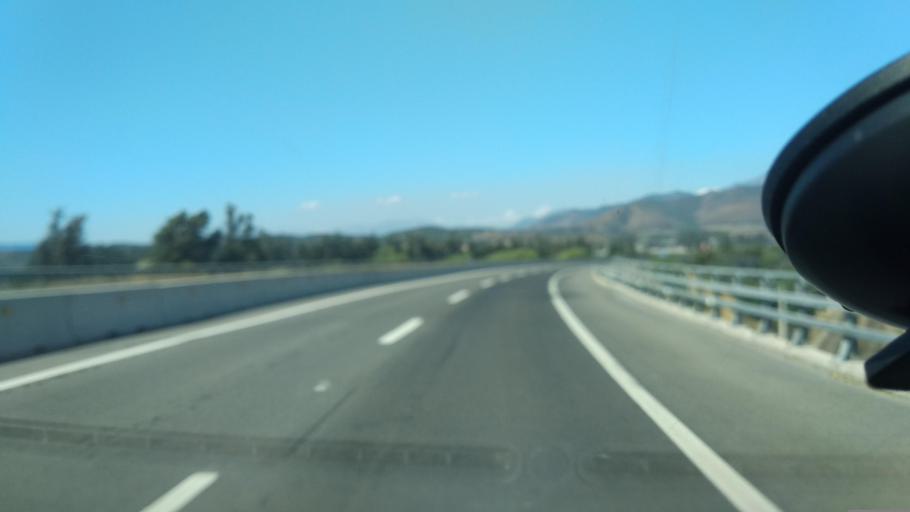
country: CL
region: Valparaiso
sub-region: Provincia de Marga Marga
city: Limache
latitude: -32.9831
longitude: -71.3169
